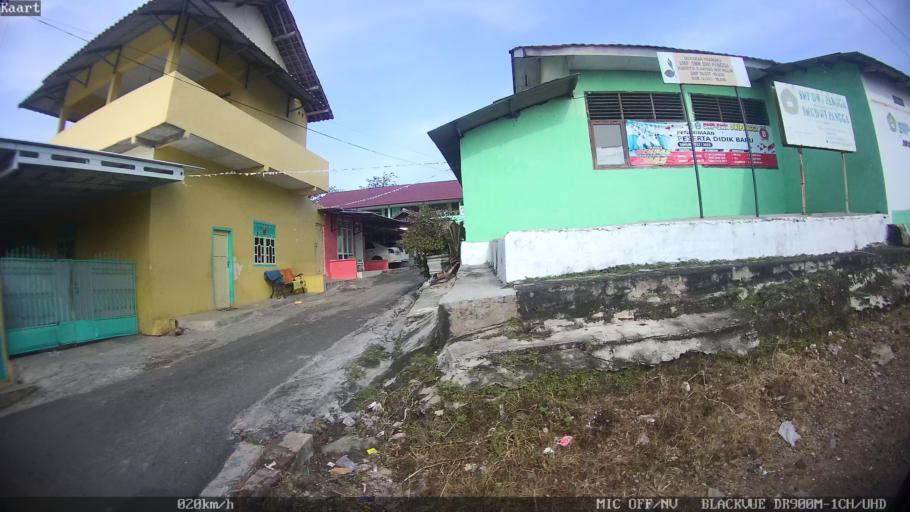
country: ID
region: Lampung
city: Kedaton
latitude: -5.3954
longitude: 105.2660
